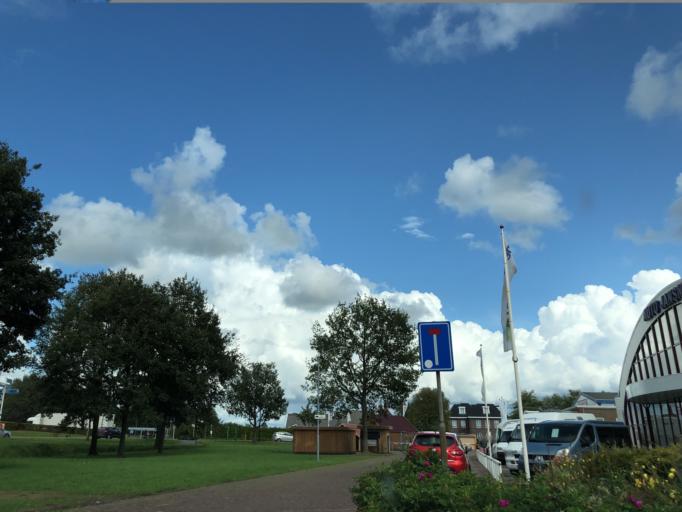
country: NL
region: Groningen
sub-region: Gemeente Grootegast
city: Grootegast
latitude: 53.1525
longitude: 6.2700
